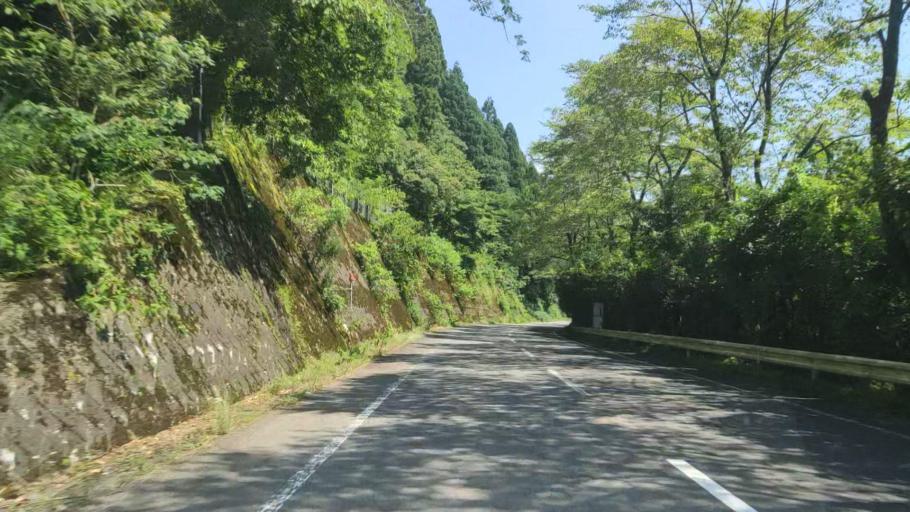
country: JP
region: Gifu
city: Godo
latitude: 35.6110
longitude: 136.6262
